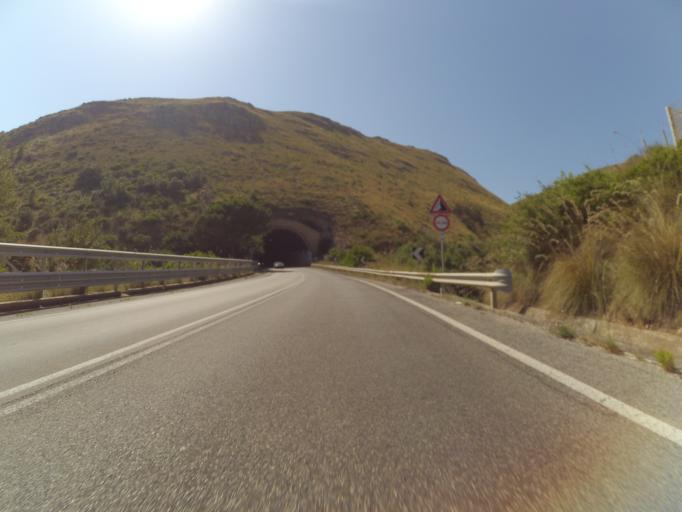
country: IT
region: Latium
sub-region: Provincia di Latina
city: Sperlonga
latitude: 41.2406
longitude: 13.4756
